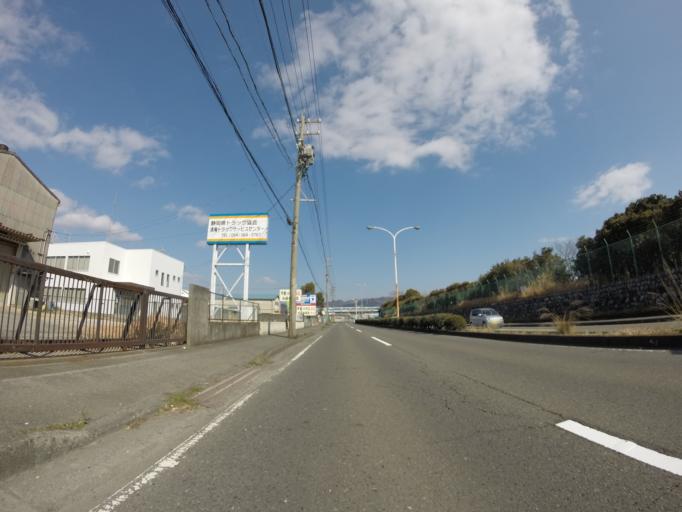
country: JP
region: Shizuoka
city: Shizuoka-shi
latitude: 35.0254
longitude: 138.4907
